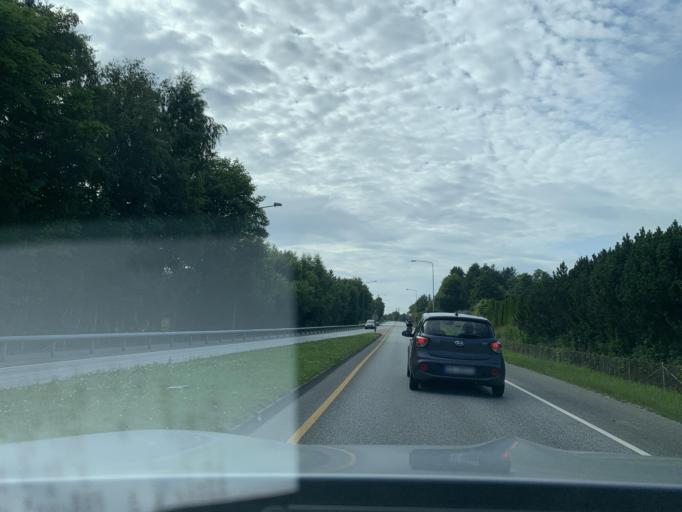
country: NO
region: Rogaland
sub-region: Stavanger
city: Stavanger
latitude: 58.9178
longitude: 5.7166
